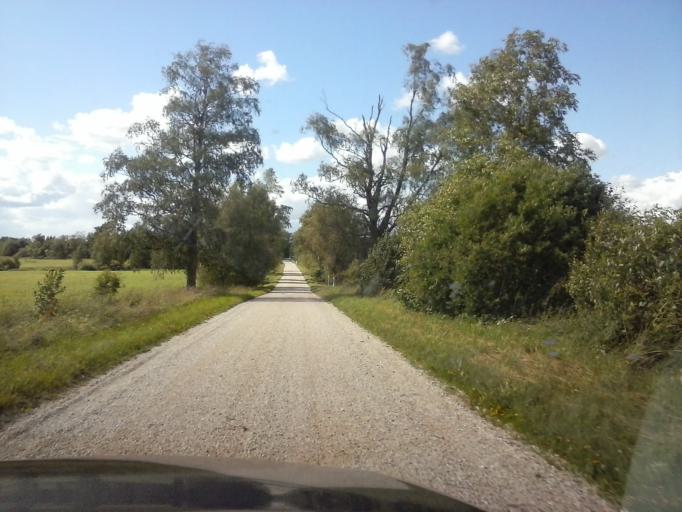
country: EE
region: Laeaene-Virumaa
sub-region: Vaeike-Maarja vald
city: Vaike-Maarja
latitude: 59.0830
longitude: 26.1892
